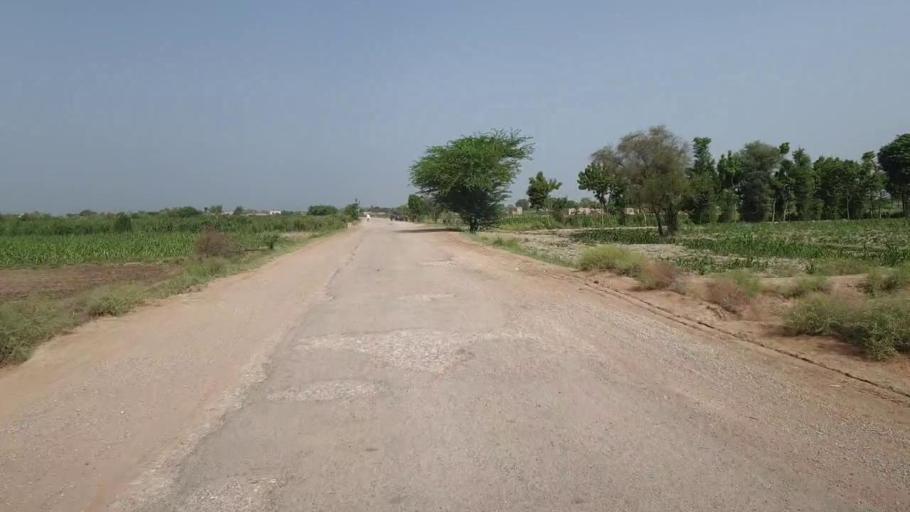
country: PK
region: Sindh
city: Daulatpur
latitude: 26.5491
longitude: 68.0598
